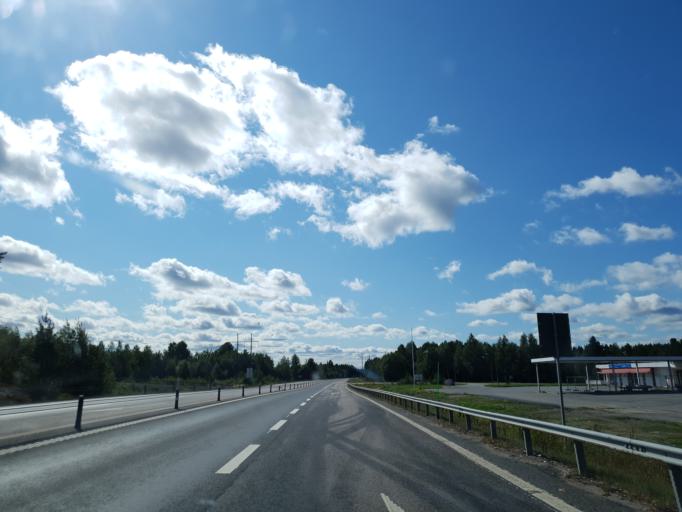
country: SE
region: Vaesterbotten
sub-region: Nordmalings Kommun
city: Nordmaling
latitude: 63.5364
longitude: 19.4018
